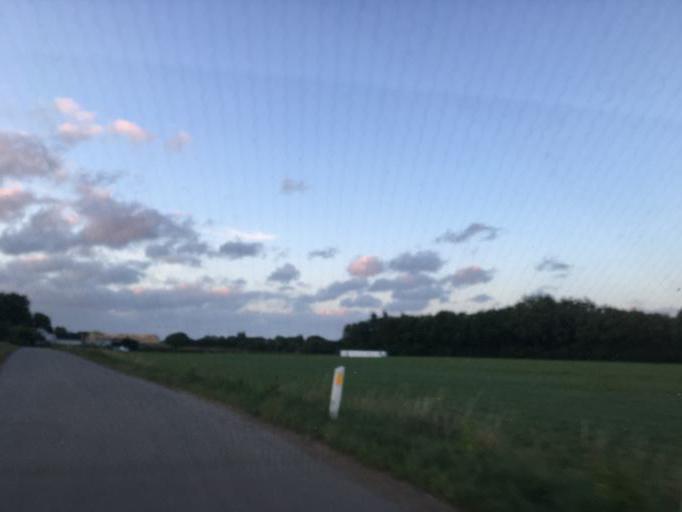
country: DK
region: Zealand
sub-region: Koge Kommune
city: Ejby
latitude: 55.5216
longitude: 12.0928
